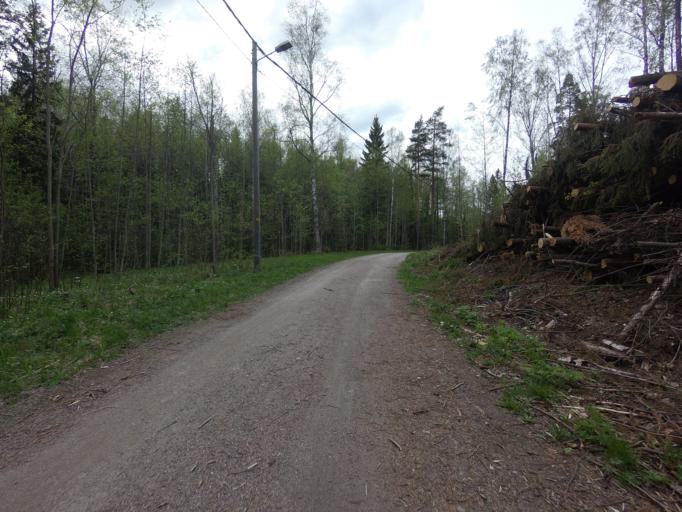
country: FI
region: Uusimaa
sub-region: Helsinki
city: Kauniainen
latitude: 60.1893
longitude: 24.7197
